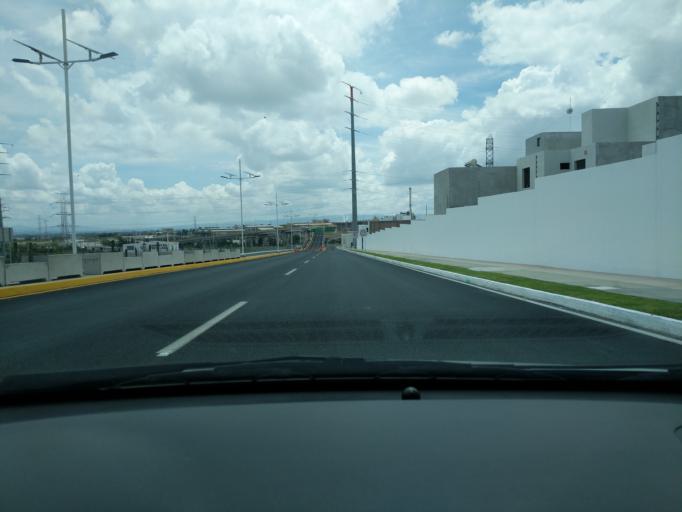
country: MX
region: San Luis Potosi
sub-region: Mexquitic de Carmona
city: Guadalupe Victoria
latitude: 22.1686
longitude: -101.0437
